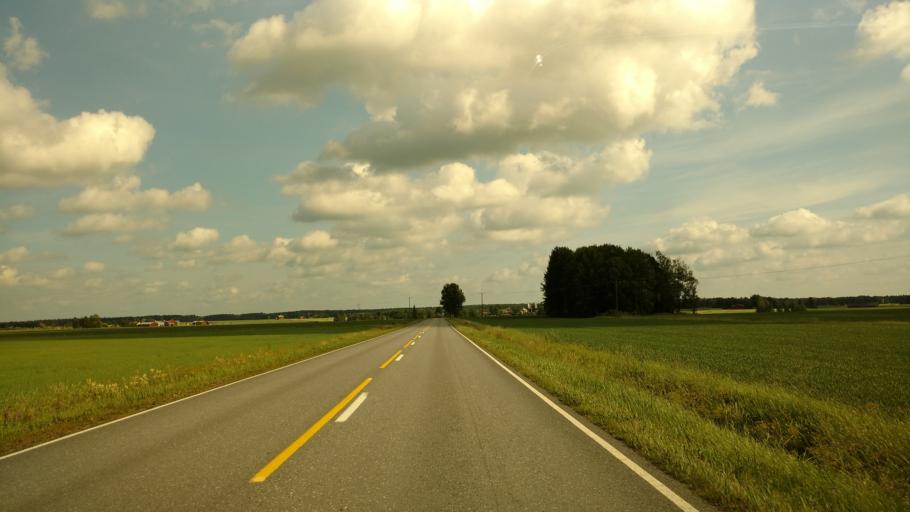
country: FI
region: Varsinais-Suomi
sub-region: Loimaa
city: Koski Tl
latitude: 60.6326
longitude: 23.1051
